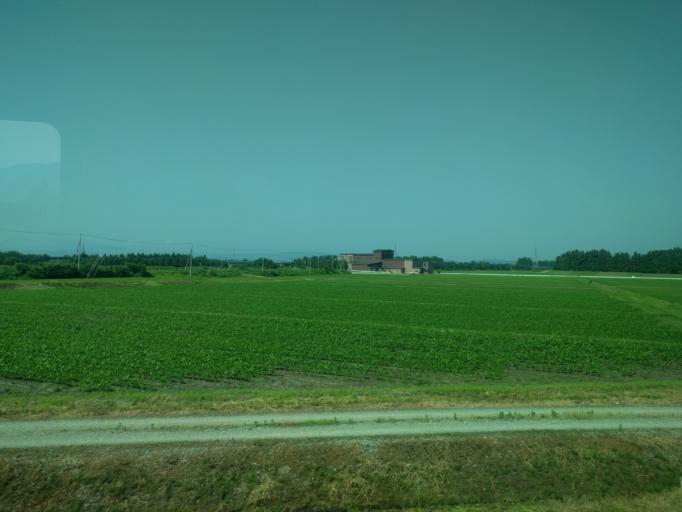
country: JP
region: Fukushima
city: Inawashiro
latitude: 37.5382
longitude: 140.1345
